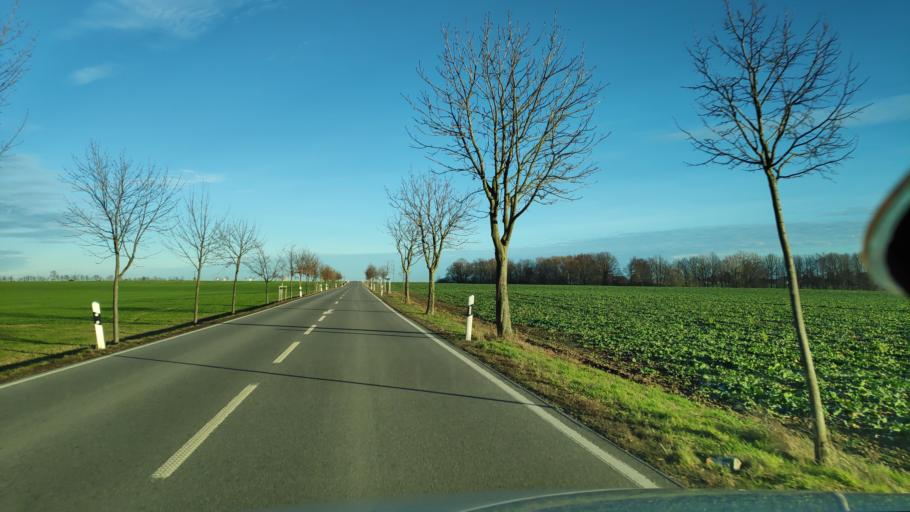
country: DE
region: Thuringia
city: Seelingstadt
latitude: 50.7984
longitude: 12.2534
